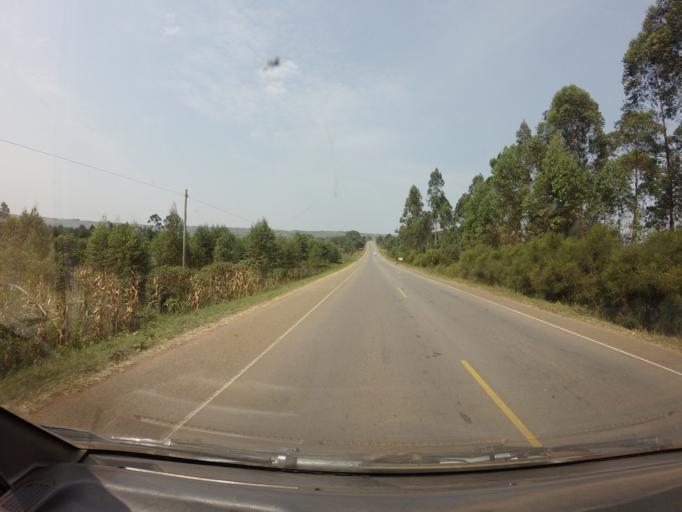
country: UG
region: Central Region
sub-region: Lwengo District
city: Lwengo
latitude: -0.3931
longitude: 31.3402
